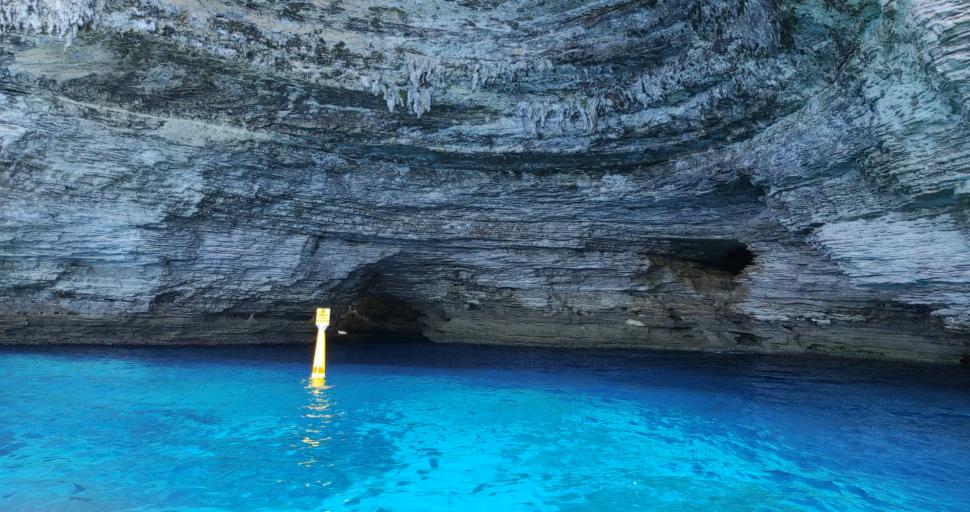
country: FR
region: Corsica
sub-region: Departement de la Corse-du-Sud
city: Bonifacio
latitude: 41.3881
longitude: 9.1429
